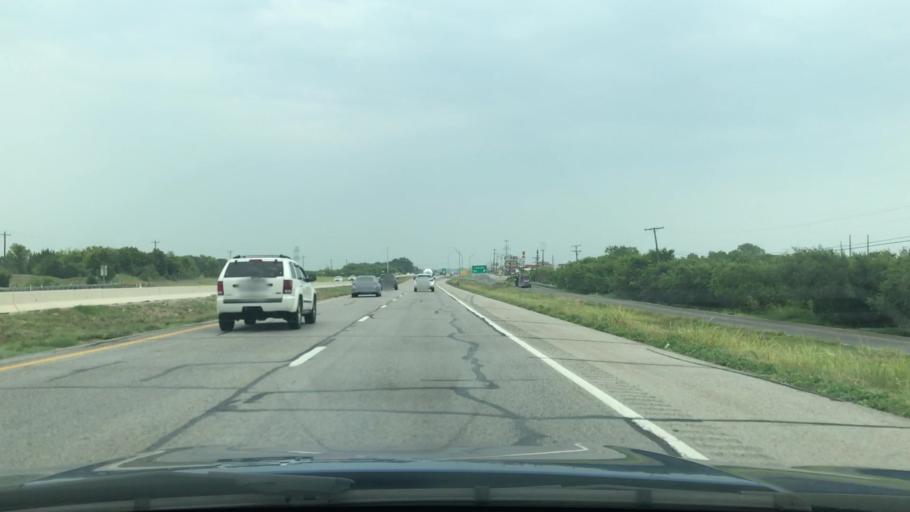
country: US
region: Texas
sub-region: Dallas County
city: Sunnyvale
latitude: 32.7786
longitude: -96.5248
